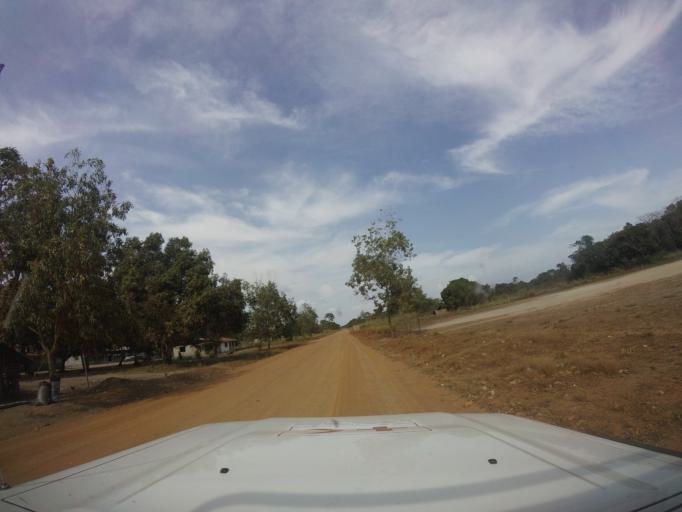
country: LR
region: Grand Cape Mount
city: Robertsport
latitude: 6.6872
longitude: -11.1196
